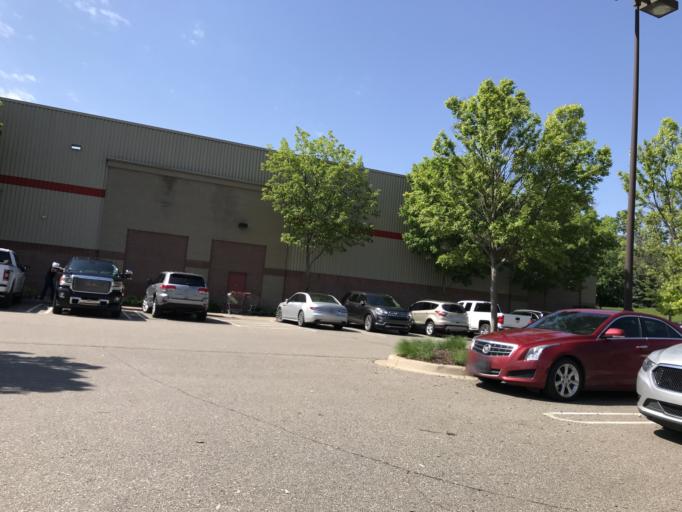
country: US
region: Michigan
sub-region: Livingston County
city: Brighton
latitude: 42.5040
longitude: -83.7625
